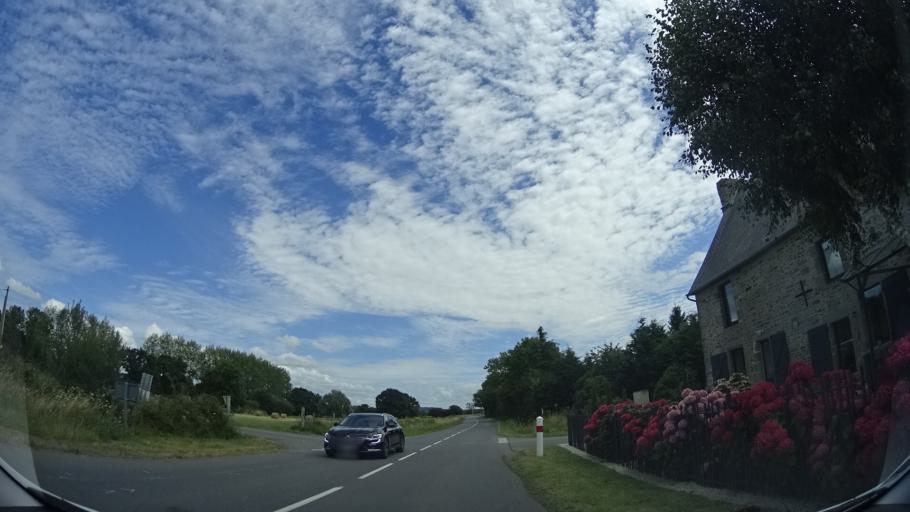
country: FR
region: Lower Normandy
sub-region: Departement de la Manche
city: Marcey-les-Greves
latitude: 48.6880
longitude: -1.4388
